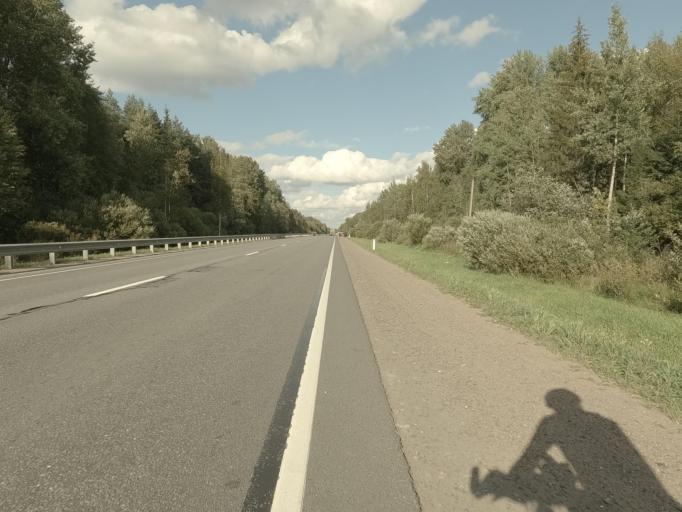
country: RU
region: Leningrad
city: Nikol'skoye
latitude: 59.6511
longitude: 30.8523
